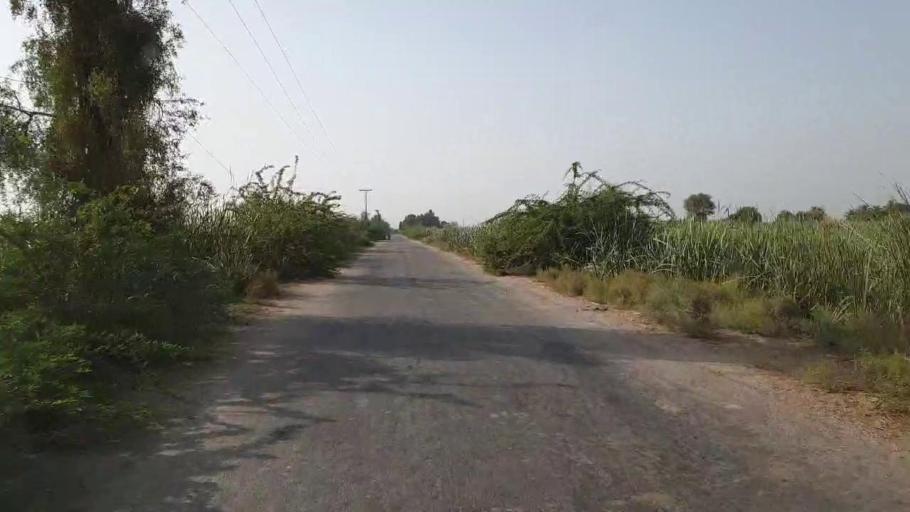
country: PK
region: Sindh
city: Jam Sahib
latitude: 26.4028
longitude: 68.8776
